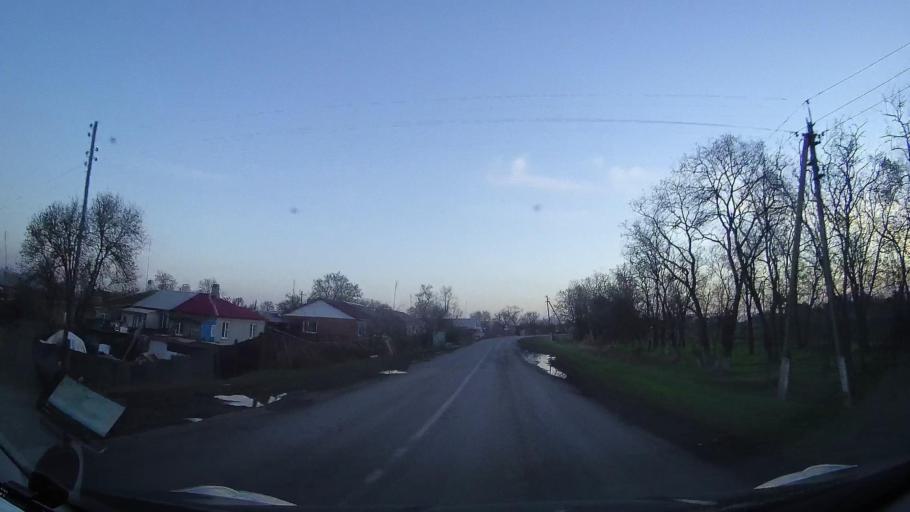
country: RU
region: Rostov
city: Zernograd
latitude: 46.9268
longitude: 40.3662
